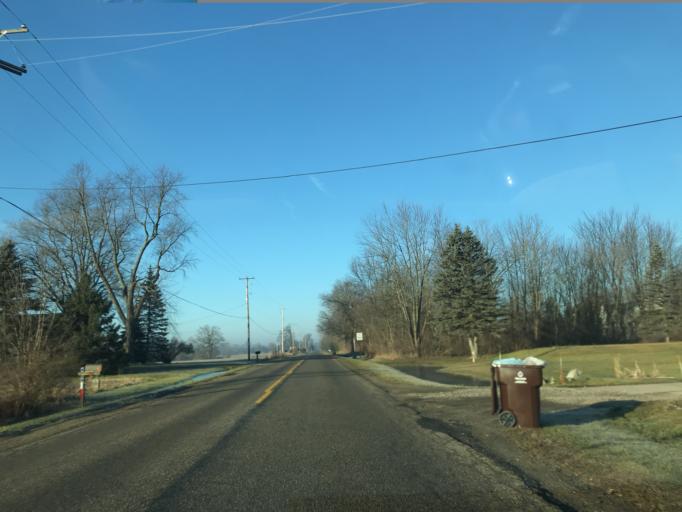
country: US
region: Michigan
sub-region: Eaton County
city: Dimondale
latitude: 42.6620
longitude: -84.6228
